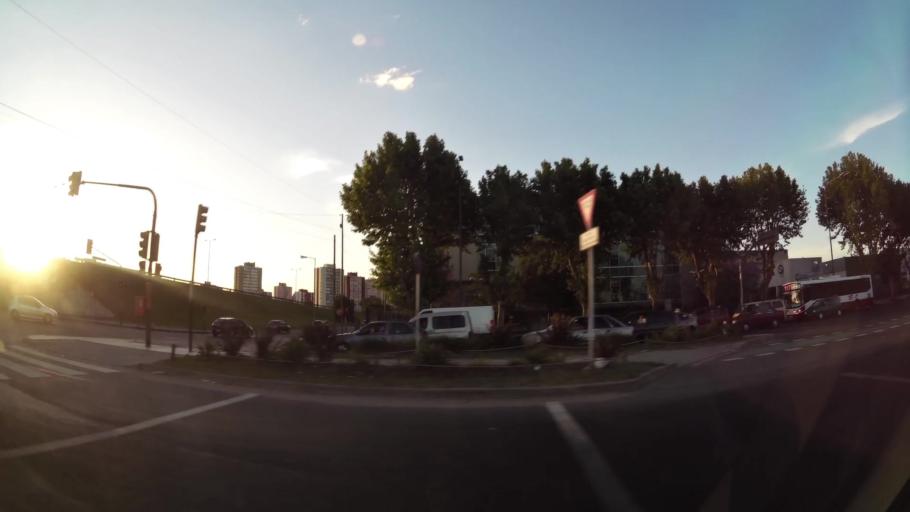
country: AR
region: Buenos Aires F.D.
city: Villa Lugano
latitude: -34.6978
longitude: -58.4697
